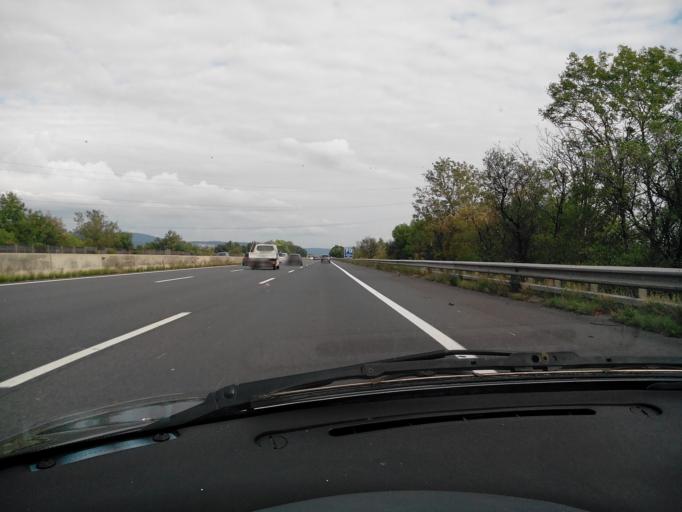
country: AT
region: Lower Austria
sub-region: Politischer Bezirk Baden
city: Leobersdorf
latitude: 47.8971
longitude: 16.2074
